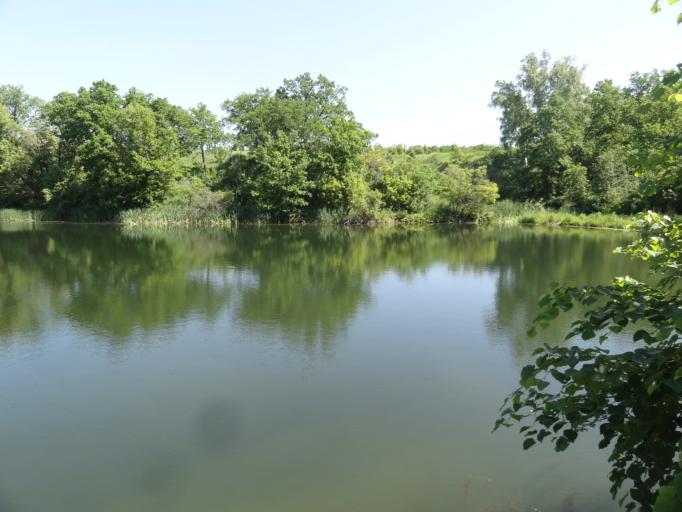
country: RU
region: Saratov
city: Krasnyy Oktyabr'
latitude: 51.2895
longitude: 45.5705
